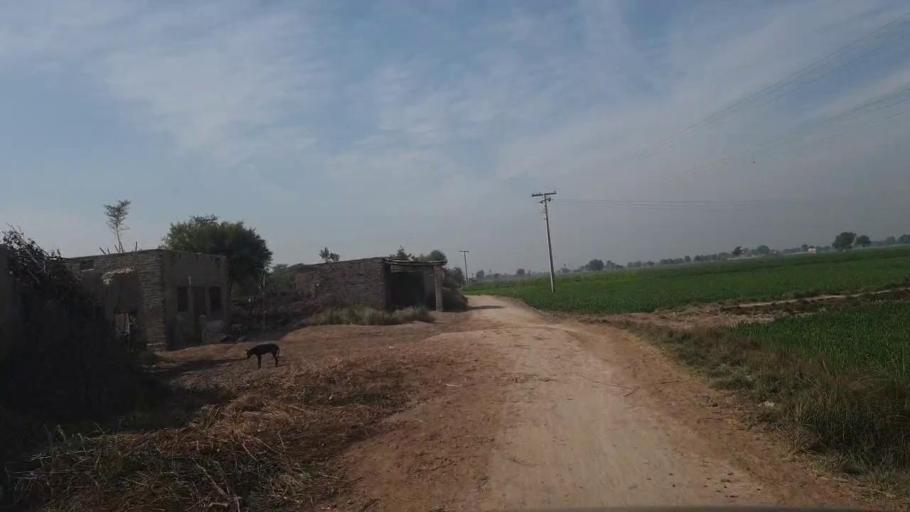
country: PK
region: Sindh
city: Nawabshah
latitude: 26.1603
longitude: 68.4940
